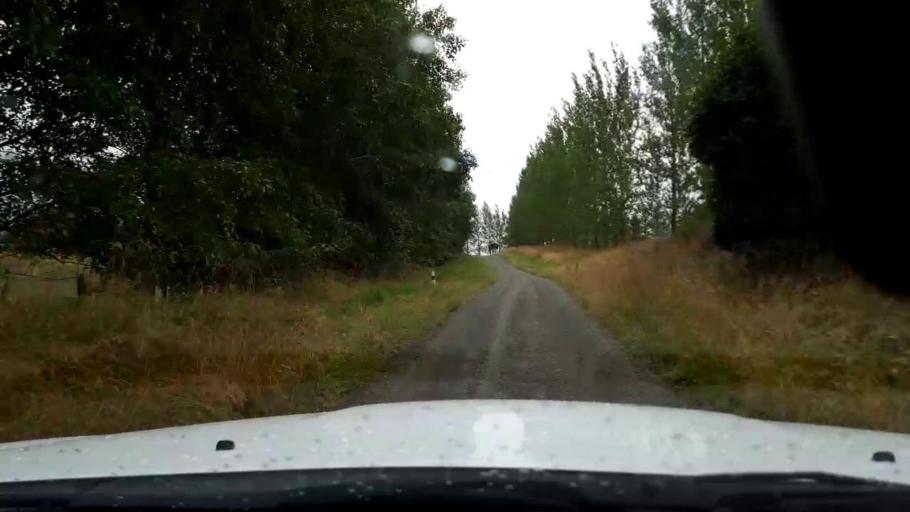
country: NZ
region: Canterbury
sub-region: Timaru District
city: Pleasant Point
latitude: -44.1062
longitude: 171.1352
